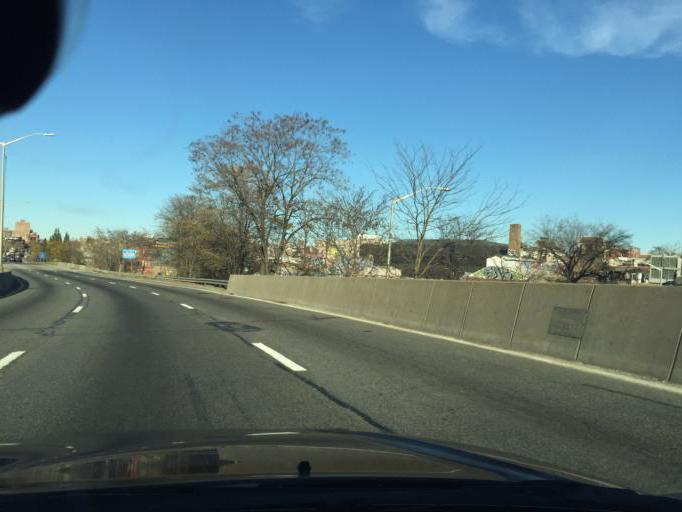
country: US
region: New York
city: New York City
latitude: 40.6969
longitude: -73.9628
